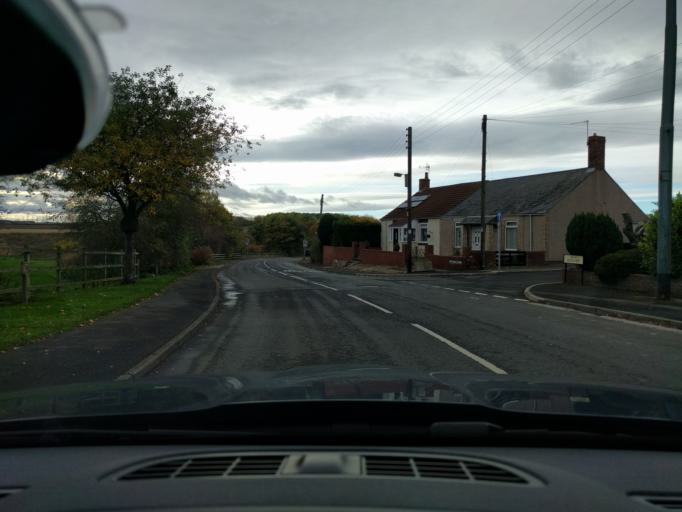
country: GB
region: England
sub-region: Northumberland
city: Ashington
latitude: 55.1447
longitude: -1.5507
